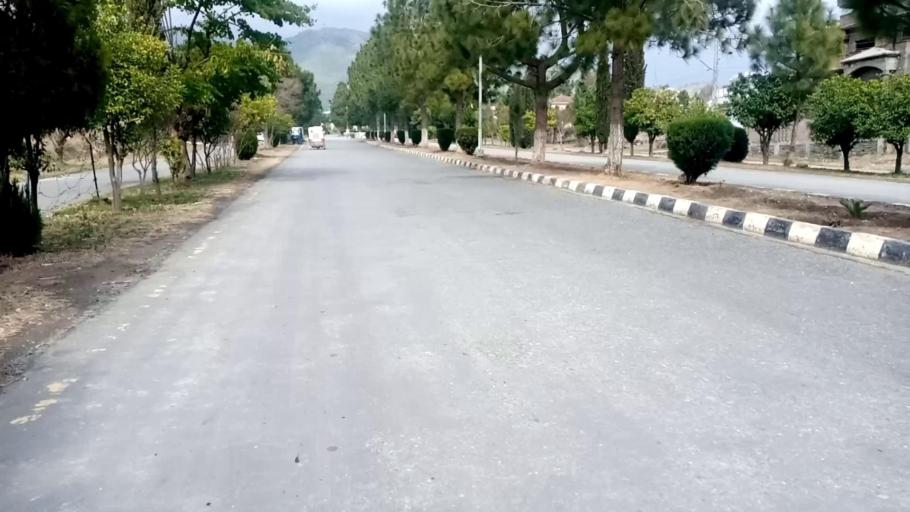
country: PK
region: Khyber Pakhtunkhwa
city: Mingora
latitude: 34.8262
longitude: 72.3407
